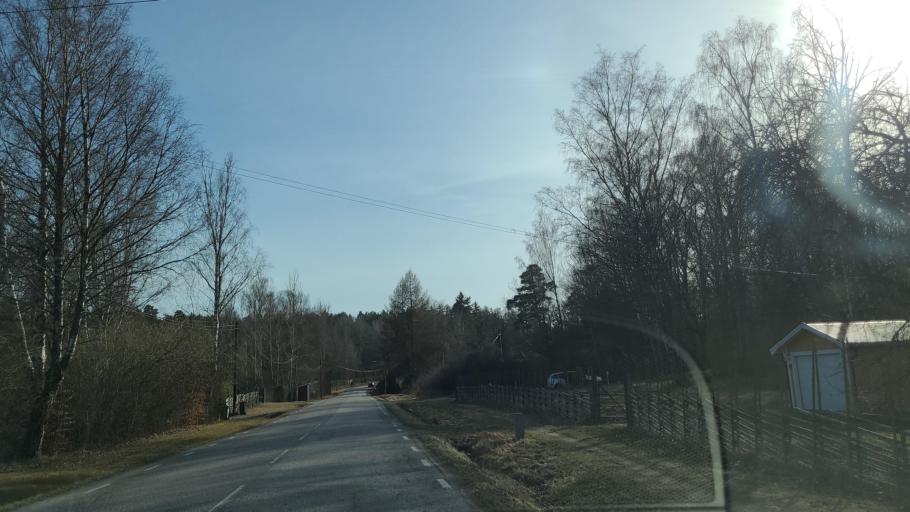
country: SE
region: Stockholm
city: Stenhamra
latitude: 59.2784
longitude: 17.7075
